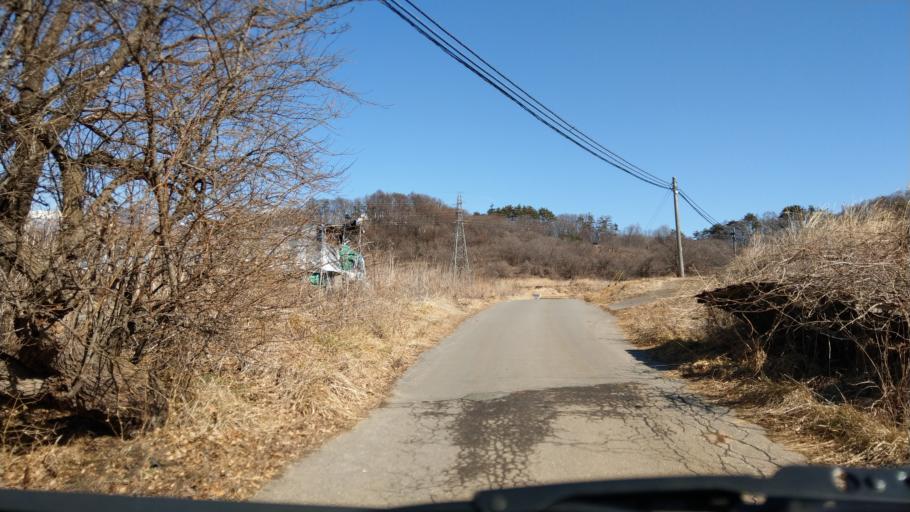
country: JP
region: Nagano
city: Komoro
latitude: 36.3120
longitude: 138.3994
